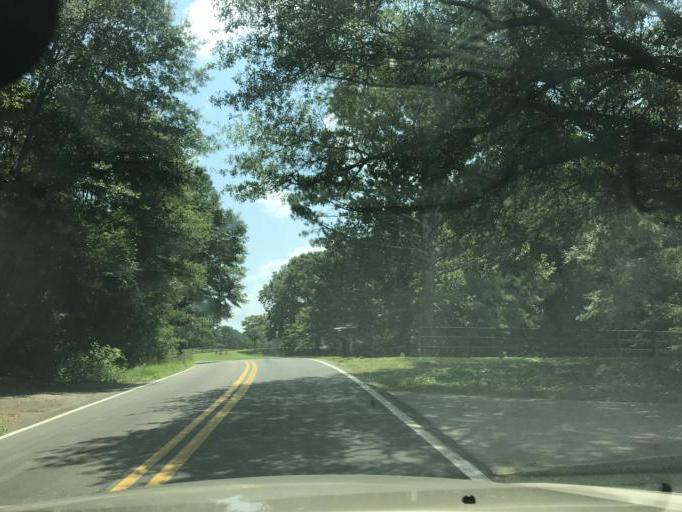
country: US
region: Georgia
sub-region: Forsyth County
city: Cumming
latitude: 34.3109
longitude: -84.1960
